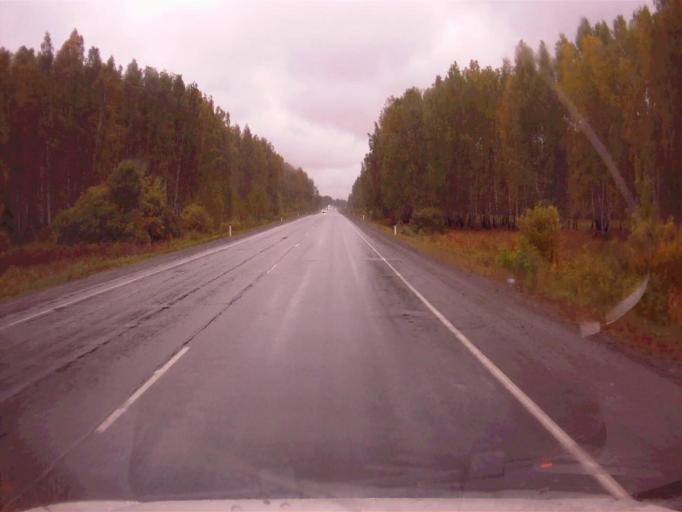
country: RU
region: Chelyabinsk
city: Argayash
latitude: 55.4647
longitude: 60.9129
